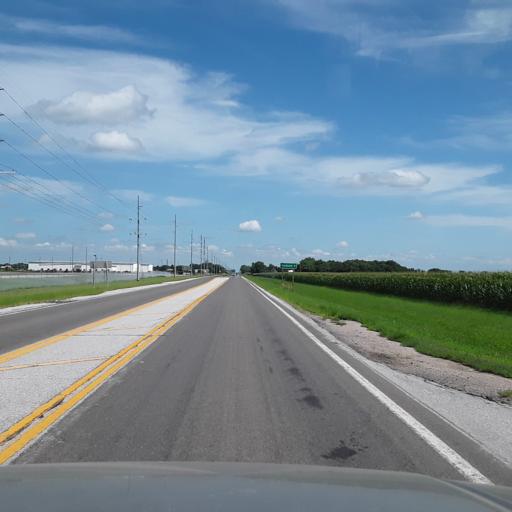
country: US
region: Nebraska
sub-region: York County
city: York
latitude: 40.9029
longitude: -97.4063
